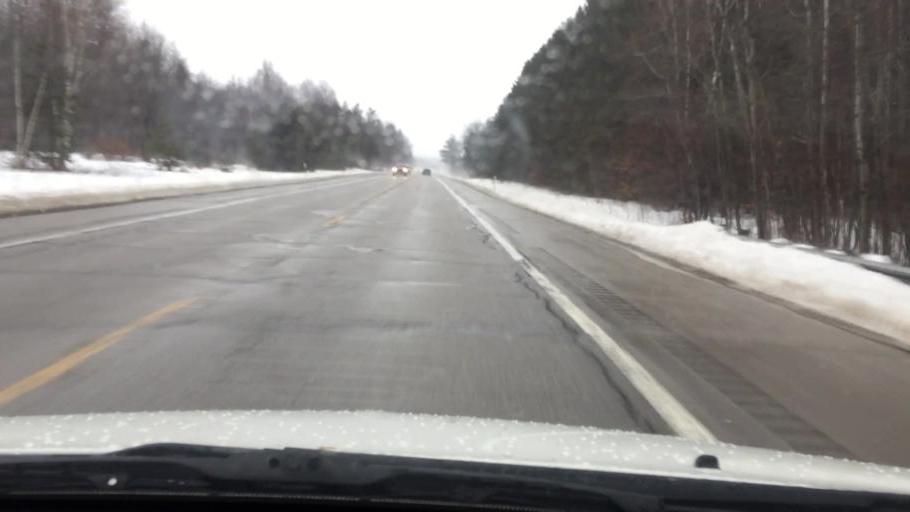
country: US
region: Michigan
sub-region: Kalkaska County
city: Kalkaska
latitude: 44.6047
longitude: -85.3241
